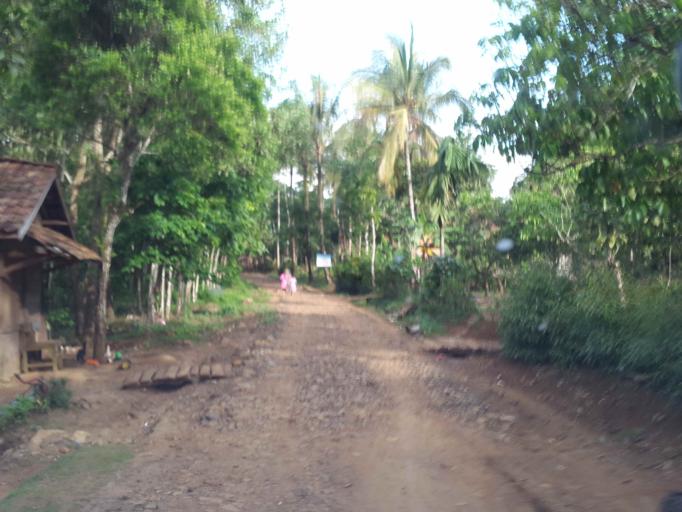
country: ID
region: Banten
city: Cibaliung
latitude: -6.7056
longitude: 105.7198
